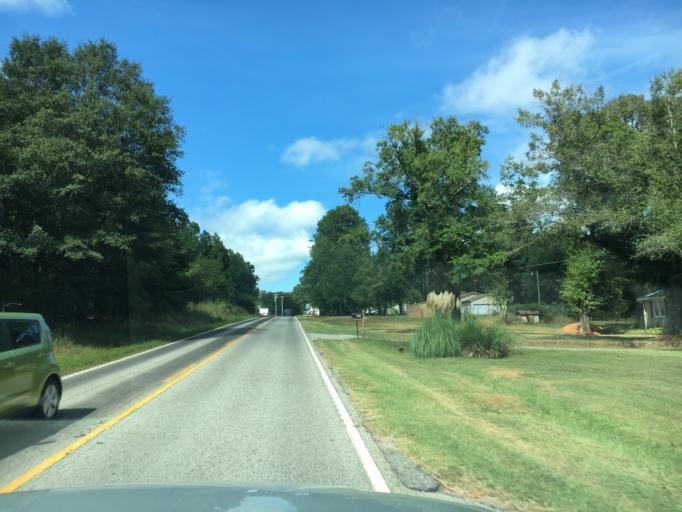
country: US
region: South Carolina
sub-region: Spartanburg County
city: Inman Mills
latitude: 35.0254
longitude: -82.1031
